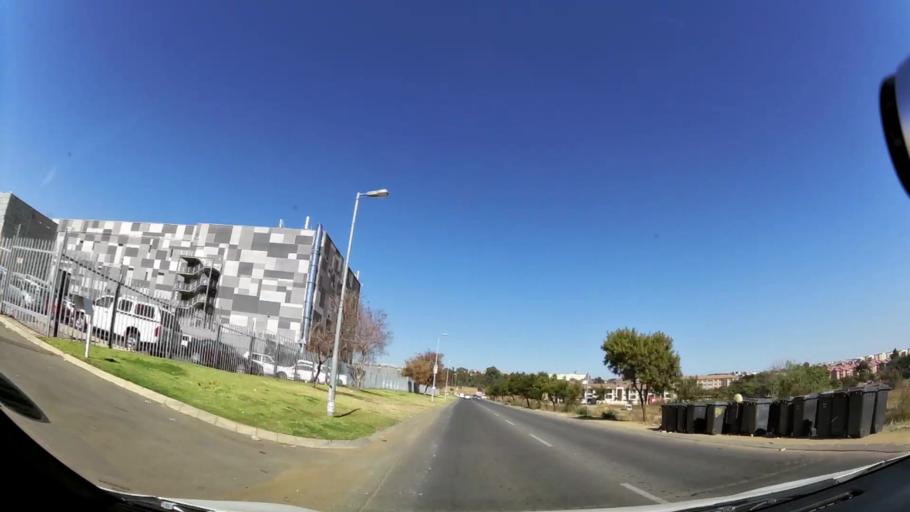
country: ZA
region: Gauteng
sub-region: City of Johannesburg Metropolitan Municipality
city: Midrand
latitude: -25.9710
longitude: 28.1255
